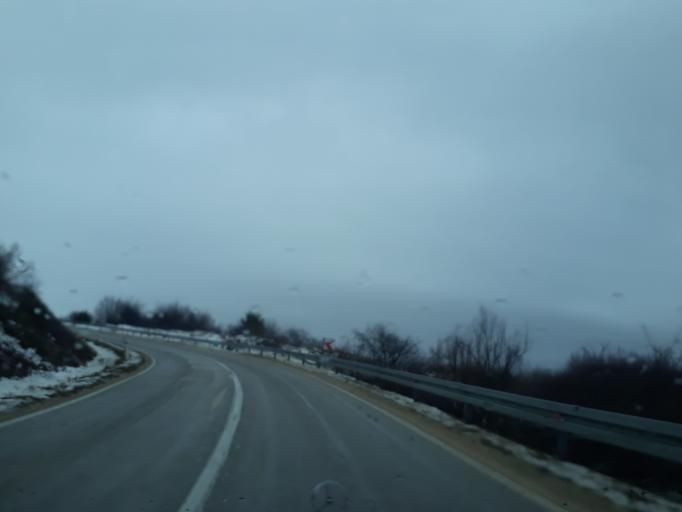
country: BA
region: Federation of Bosnia and Herzegovina
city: Tomislavgrad
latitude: 43.8013
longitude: 17.2054
